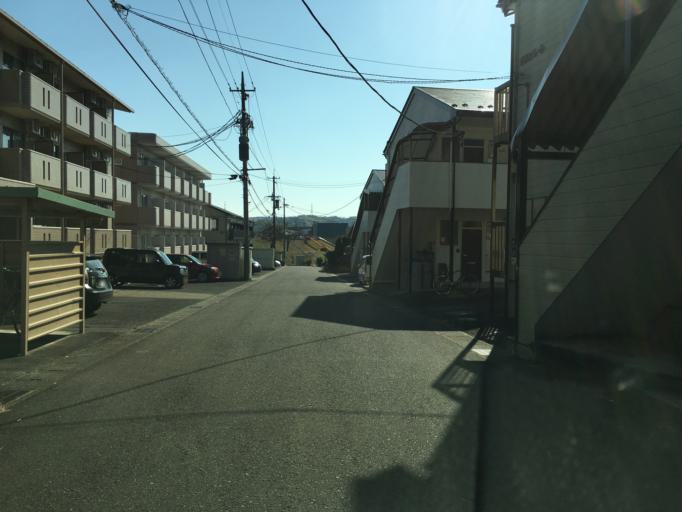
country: JP
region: Fukushima
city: Fukushima-shi
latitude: 37.6821
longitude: 140.4531
